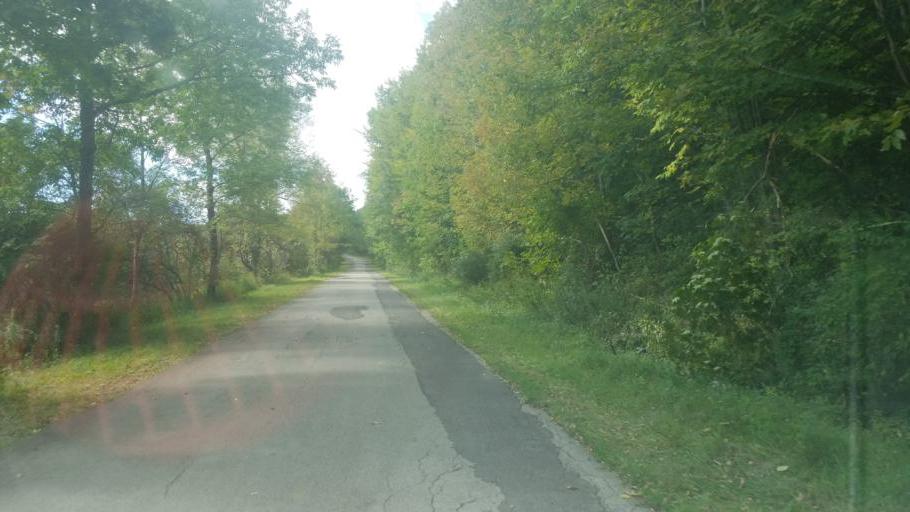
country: US
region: New York
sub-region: Cattaraugus County
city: Franklinville
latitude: 42.2309
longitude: -78.4106
